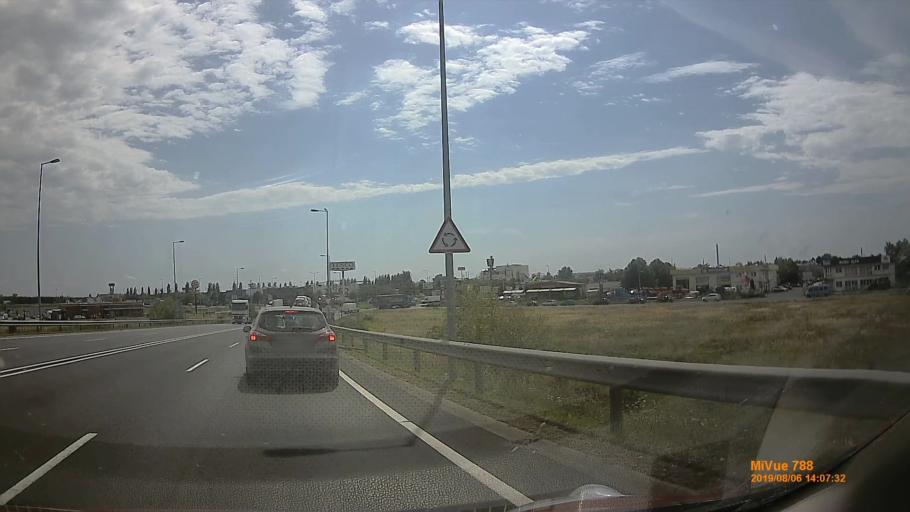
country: HU
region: Vas
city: Szombathely
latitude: 47.2441
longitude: 16.6542
